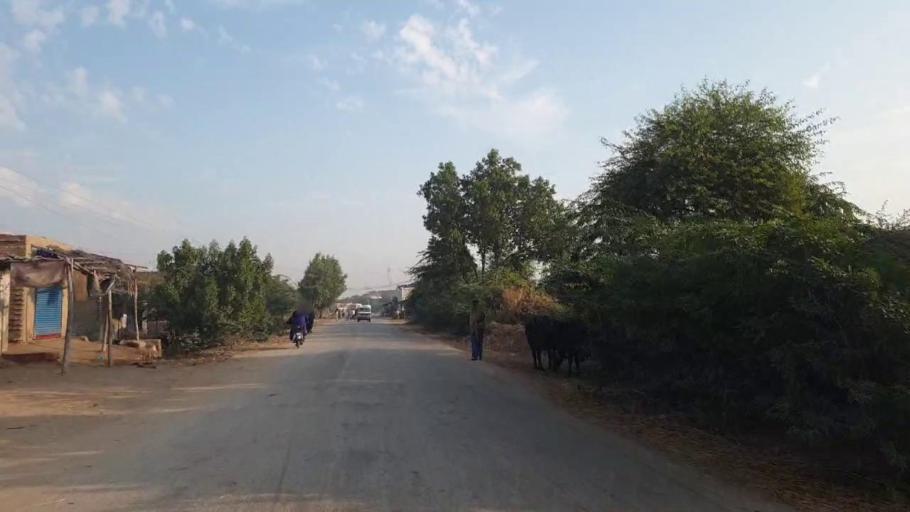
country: PK
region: Sindh
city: Tando Bago
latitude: 24.7808
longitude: 68.9630
